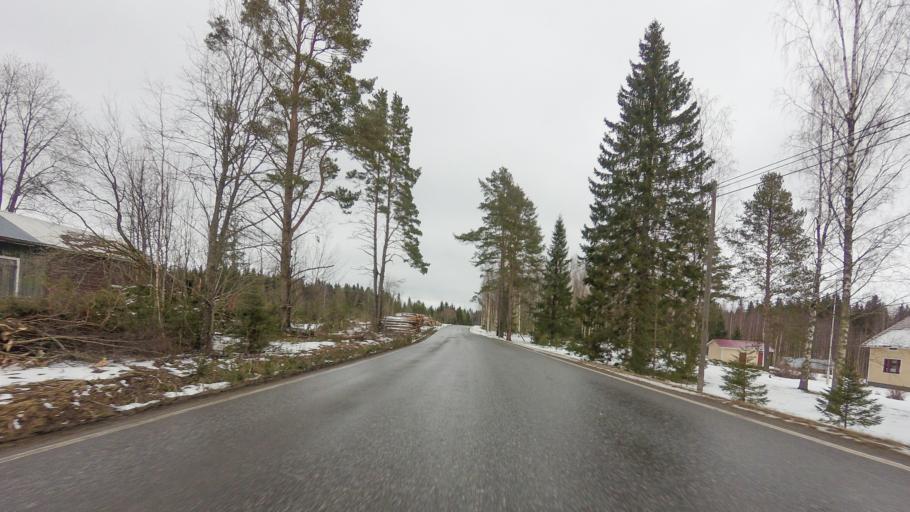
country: FI
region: Southern Savonia
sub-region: Savonlinna
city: Savonlinna
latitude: 61.9298
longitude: 28.8810
